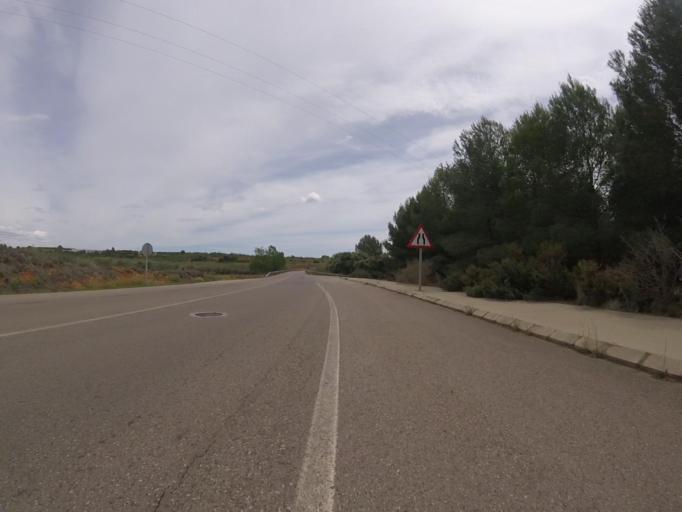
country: ES
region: Valencia
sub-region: Provincia de Castello
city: Cabanes
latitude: 40.1711
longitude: -0.0054
